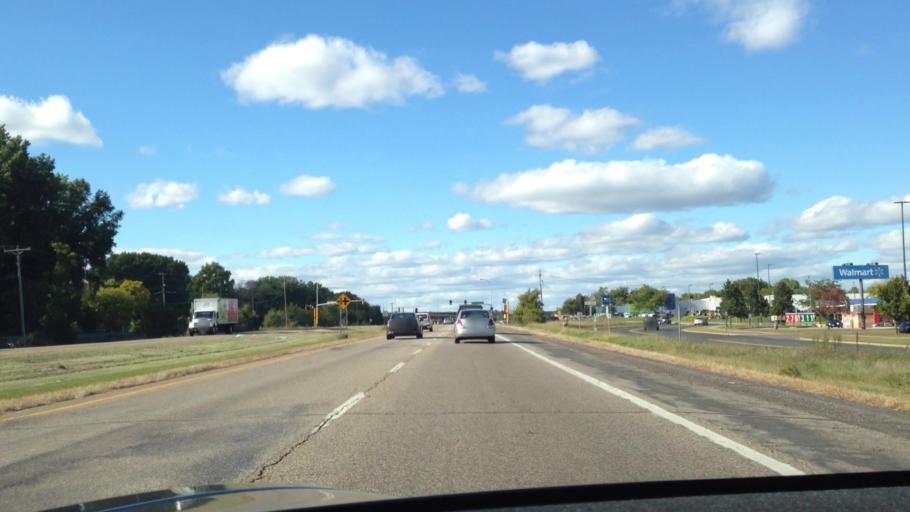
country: US
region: Minnesota
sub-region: Hennepin County
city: Osseo
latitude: 45.0990
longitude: -93.3874
